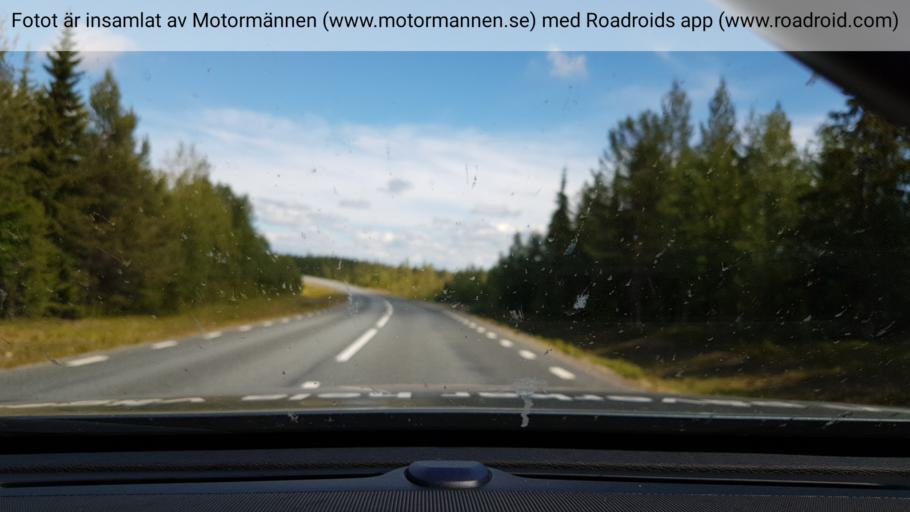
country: SE
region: Vaesterbotten
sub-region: Sorsele Kommun
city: Sorsele
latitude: 65.5577
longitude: 17.9246
